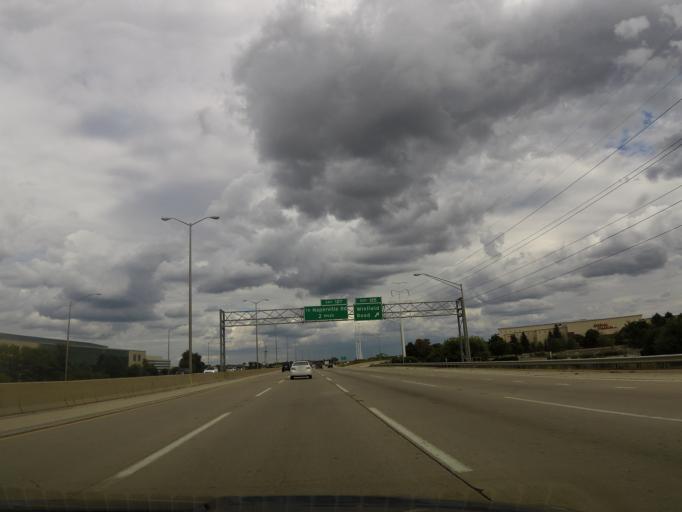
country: US
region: Illinois
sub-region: DuPage County
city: Warrenville
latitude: 41.8060
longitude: -88.1744
